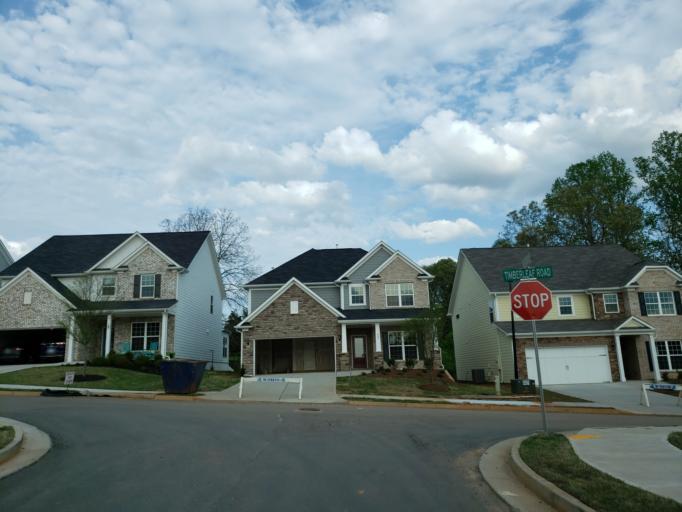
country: US
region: Georgia
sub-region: Cherokee County
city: Holly Springs
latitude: 34.1670
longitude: -84.4270
